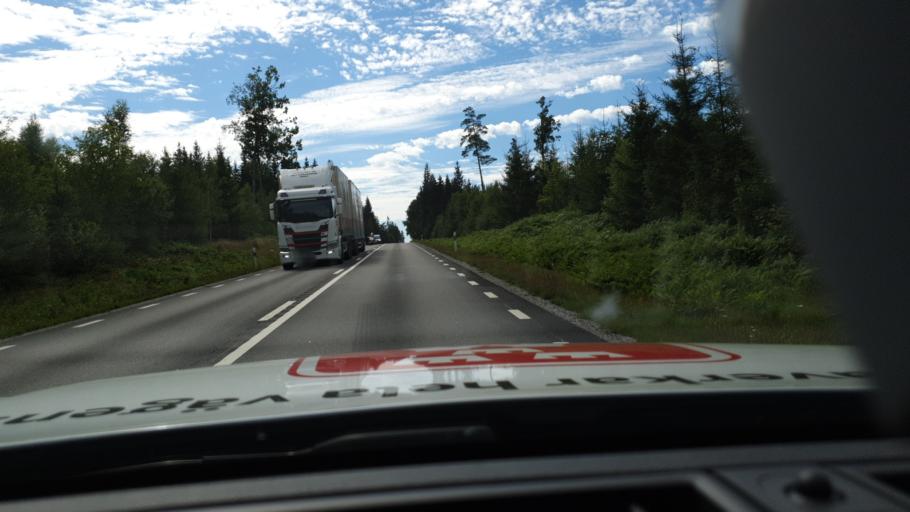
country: SE
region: Joenkoeping
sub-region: Savsjo Kommun
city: Stockaryd
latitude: 57.2663
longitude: 14.5240
